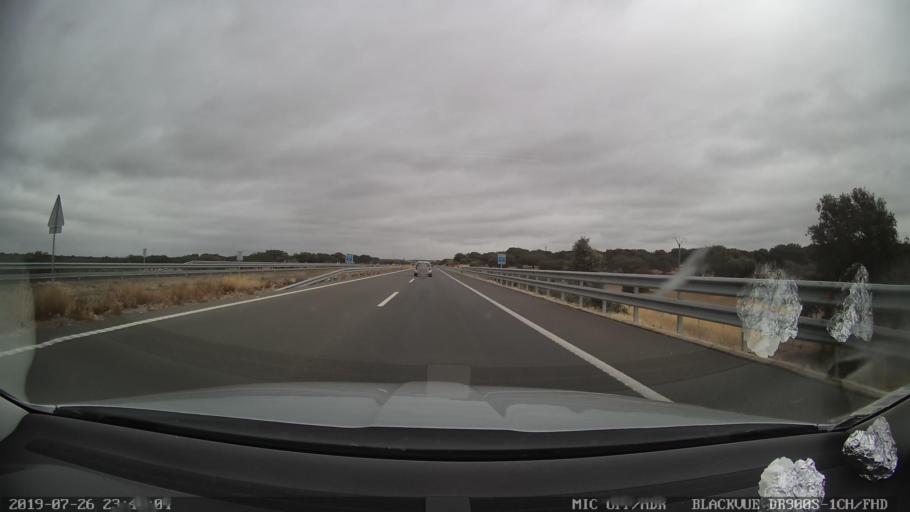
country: ES
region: Extremadura
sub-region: Provincia de Caceres
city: Torrecillas de la Tiesa
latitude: 39.5398
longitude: -5.8333
